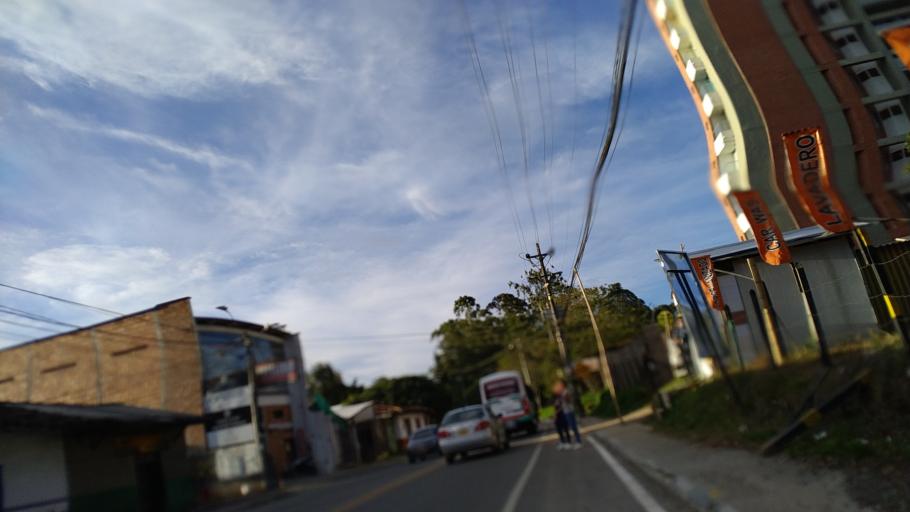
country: CO
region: Antioquia
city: Rionegro
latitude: 6.1333
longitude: -75.3785
